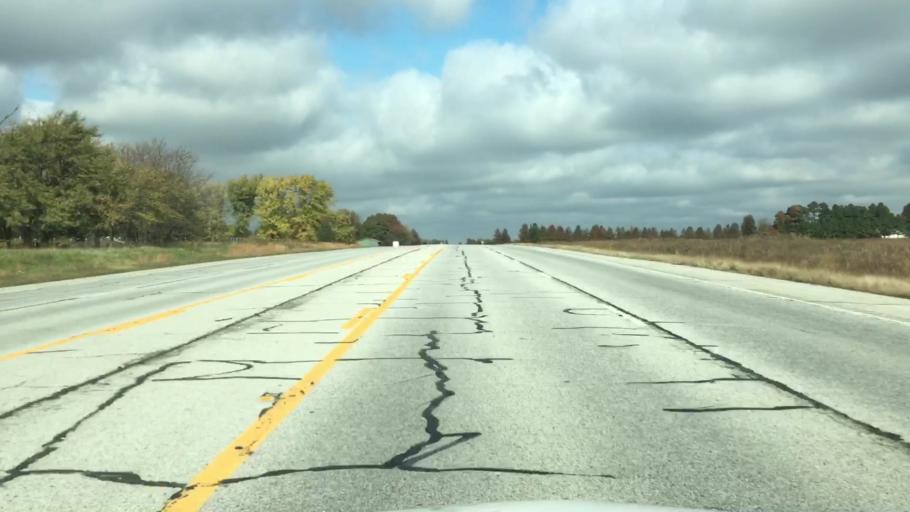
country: US
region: Arkansas
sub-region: Benton County
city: Siloam Springs
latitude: 36.2042
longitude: -94.4958
